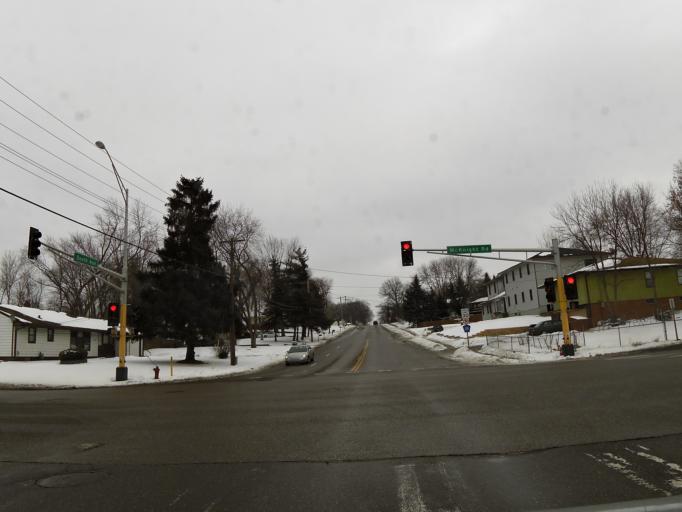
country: US
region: Minnesota
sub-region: Ramsey County
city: North Saint Paul
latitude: 45.0064
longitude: -93.0052
